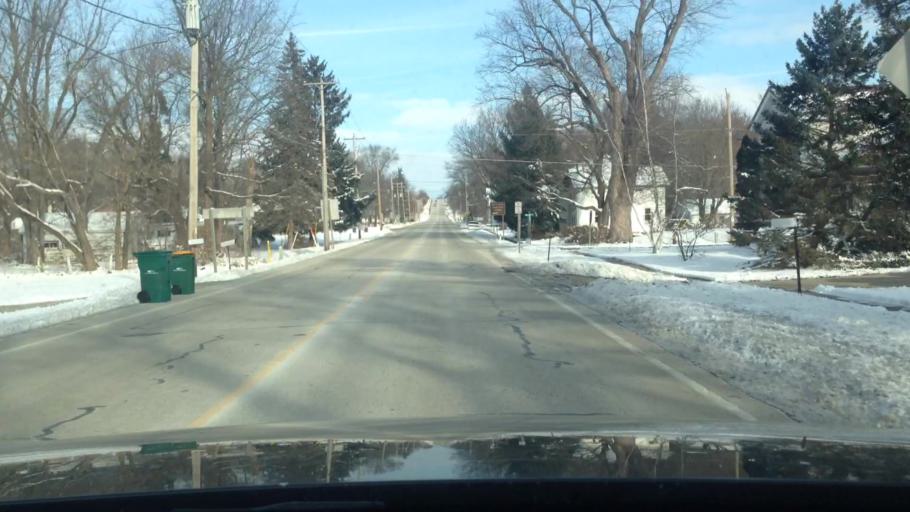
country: US
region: Wisconsin
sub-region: Walworth County
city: Lake Geneva
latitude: 42.6411
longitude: -88.4136
